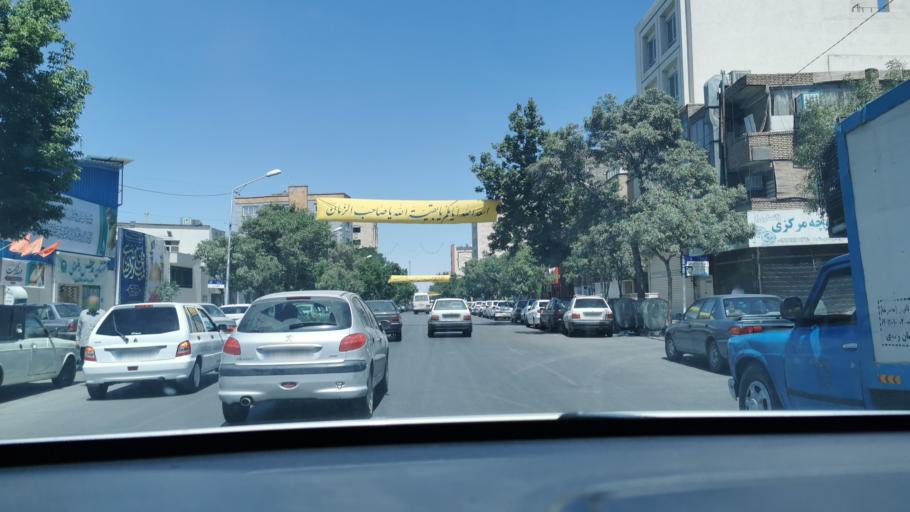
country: IR
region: Razavi Khorasan
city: Mashhad
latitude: 36.2998
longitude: 59.6109
